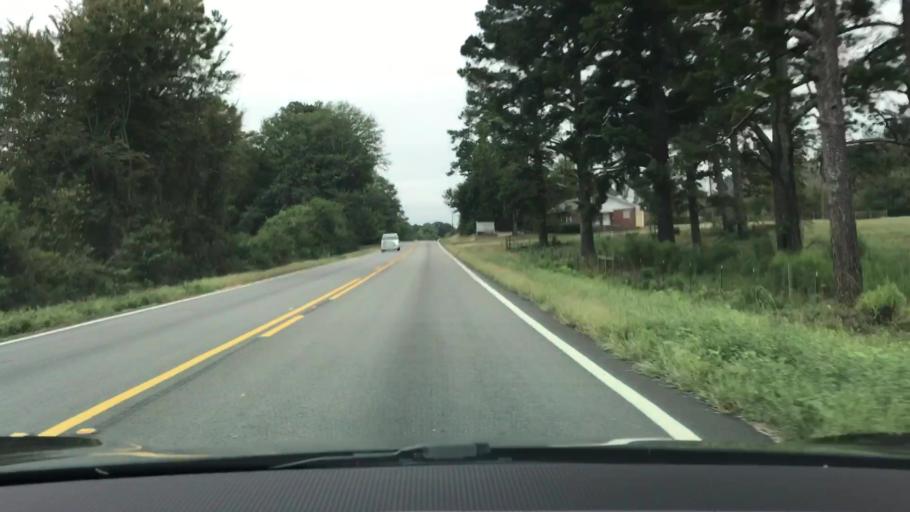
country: US
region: Georgia
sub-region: Greene County
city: Greensboro
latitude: 33.5662
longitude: -83.1537
